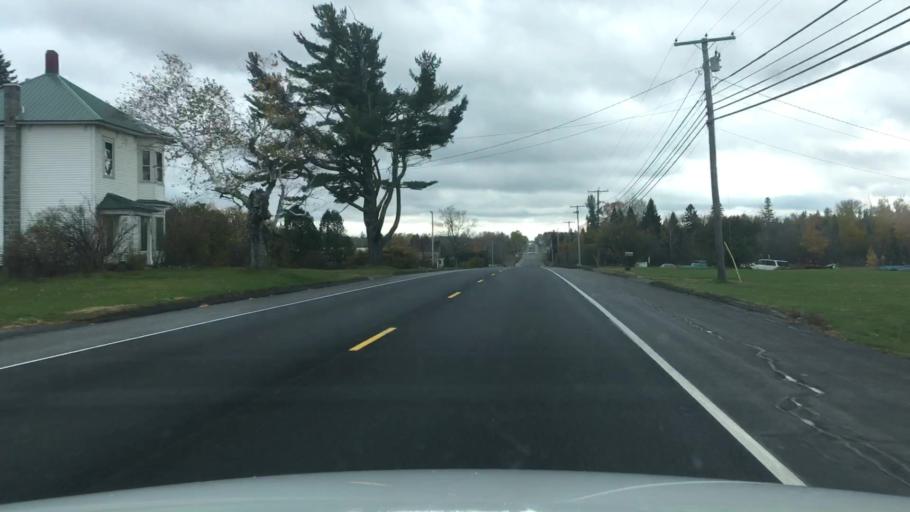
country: US
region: Maine
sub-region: Aroostook County
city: Houlton
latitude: 46.2488
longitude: -67.8408
